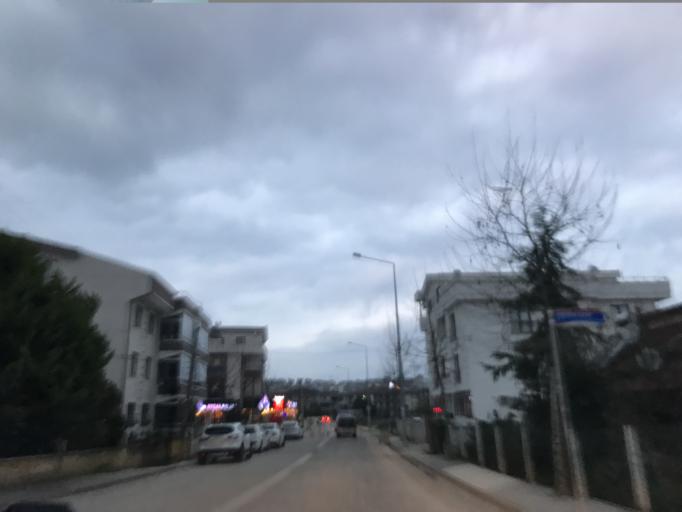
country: TR
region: Yalova
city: Yalova
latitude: 40.6400
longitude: 29.2614
